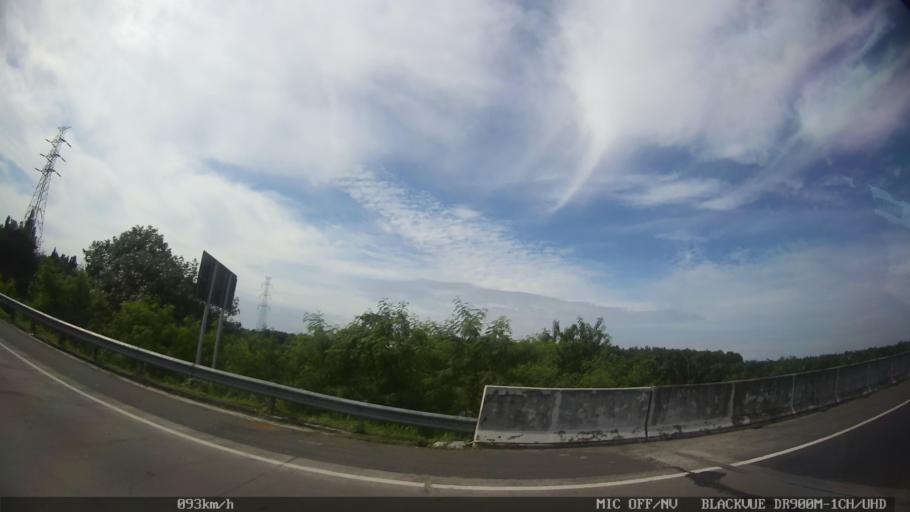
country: ID
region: North Sumatra
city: Sunggal
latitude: 3.6373
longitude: 98.5903
